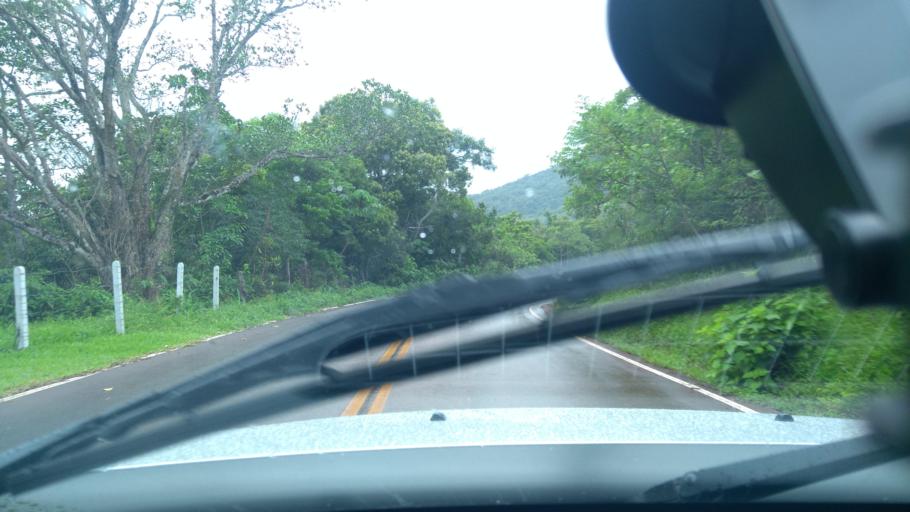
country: BR
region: Rio Grande do Sul
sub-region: Torres
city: Torres
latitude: -29.1826
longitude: -49.9862
